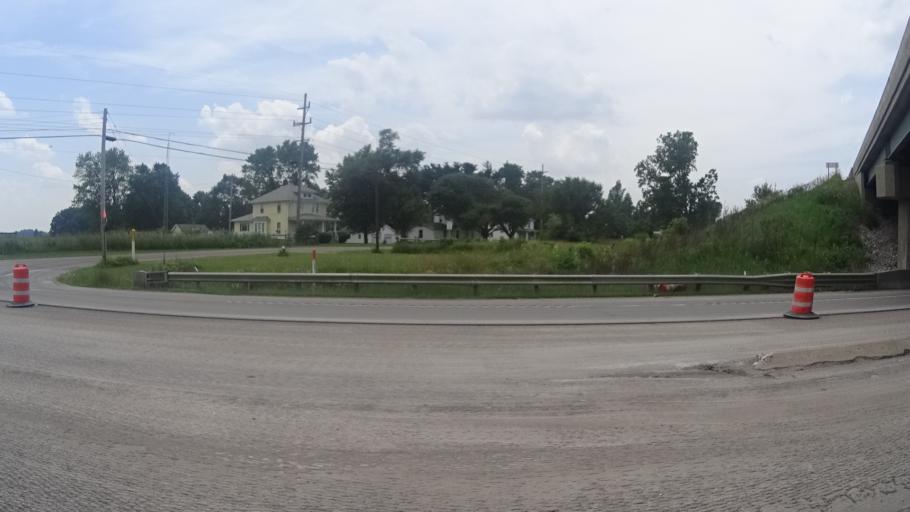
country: US
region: Ohio
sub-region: Erie County
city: Milan
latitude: 41.3226
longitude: -82.6161
